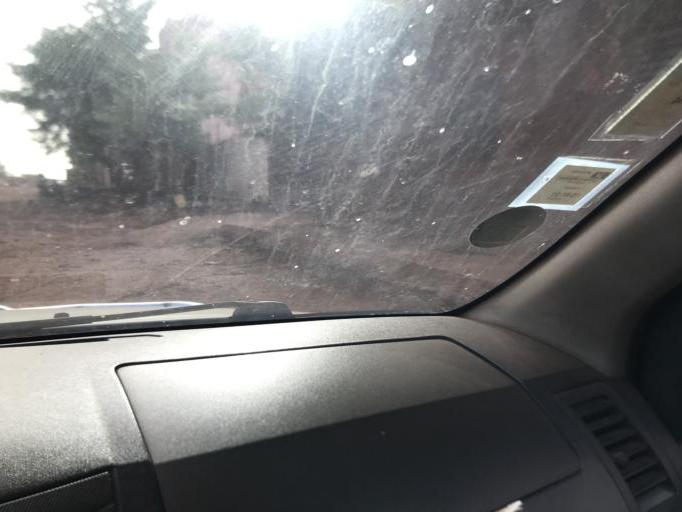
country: ML
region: Bamako
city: Bamako
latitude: 12.5826
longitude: -7.9987
